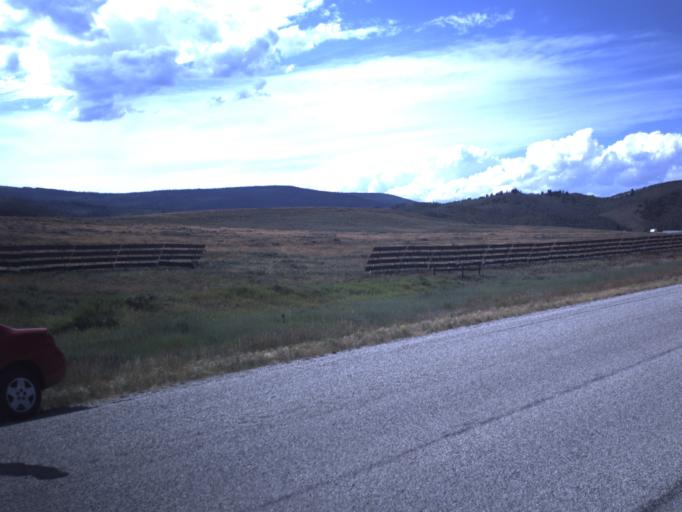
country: US
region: Utah
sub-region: Wasatch County
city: Heber
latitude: 40.2722
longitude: -111.2132
